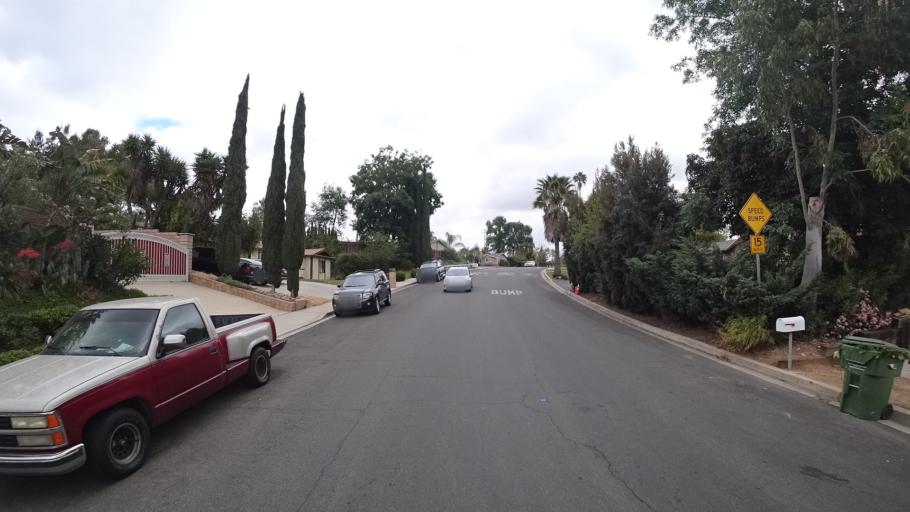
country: US
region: California
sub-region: Ventura County
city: Thousand Oaks
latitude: 34.2105
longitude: -118.8581
